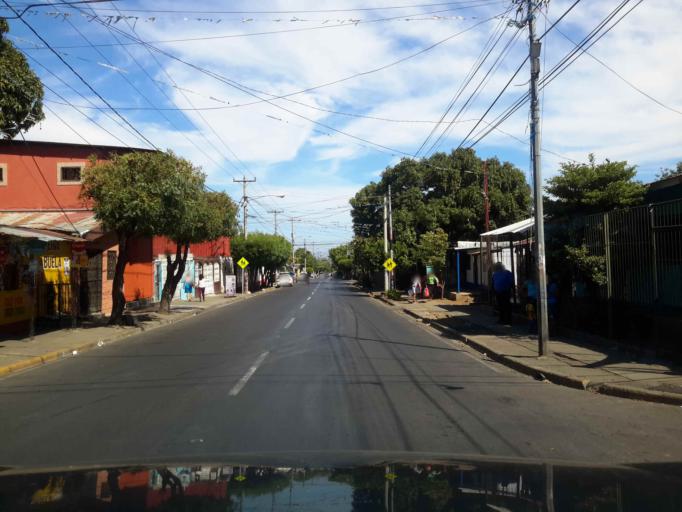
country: NI
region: Managua
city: Managua
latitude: 12.1187
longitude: -86.2964
